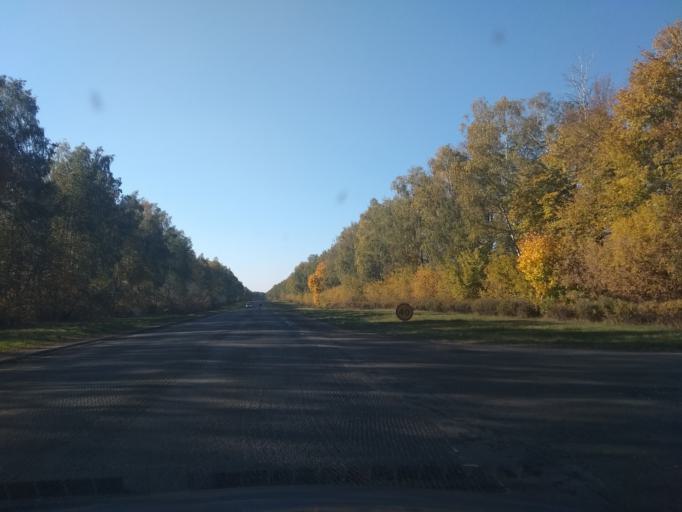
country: BY
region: Grodnenskaya
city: Zhyrovichy
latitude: 53.0581
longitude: 25.4535
